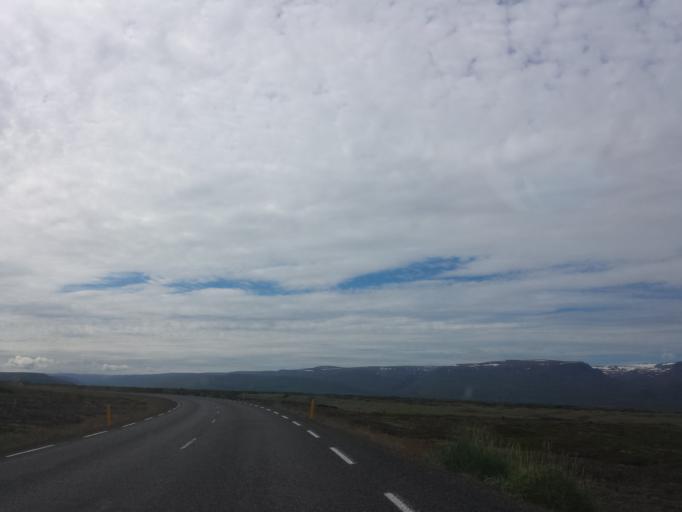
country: IS
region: Northeast
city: Husavik
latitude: 65.9633
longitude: -17.4237
